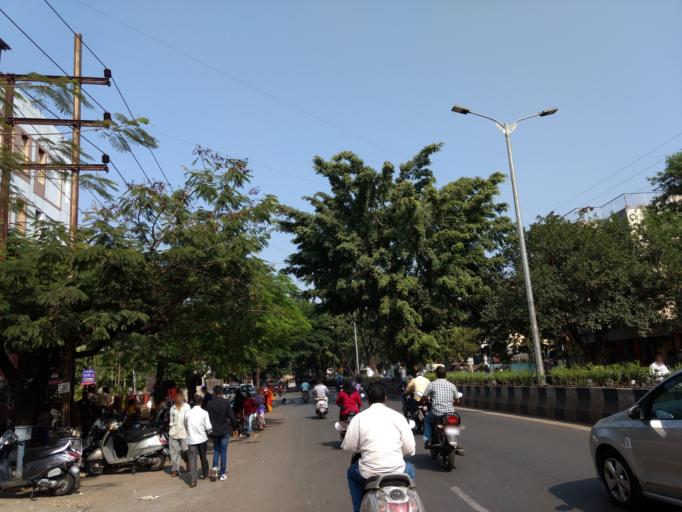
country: IN
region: Maharashtra
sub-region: Pune Division
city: Pune
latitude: 18.4756
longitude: 73.8624
